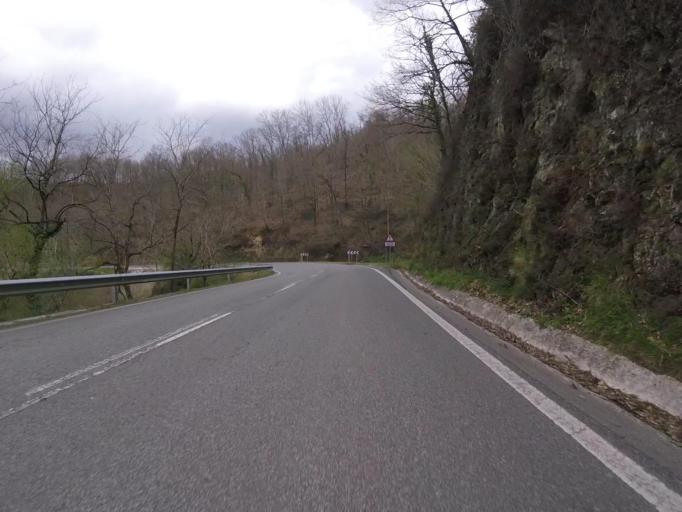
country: ES
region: Navarre
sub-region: Provincia de Navarra
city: Etxalar
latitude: 43.2408
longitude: -1.6660
